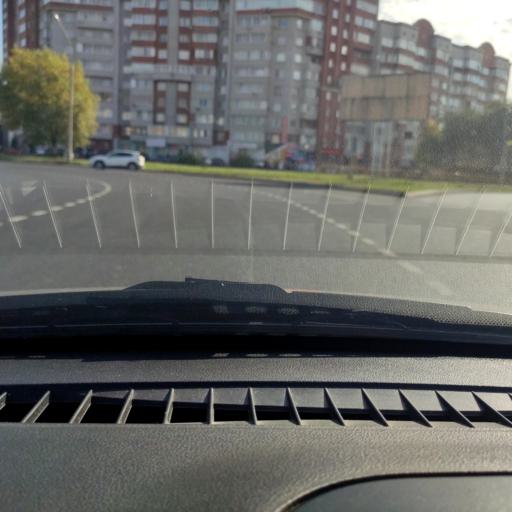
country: RU
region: Samara
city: Tol'yatti
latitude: 53.5422
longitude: 49.3303
